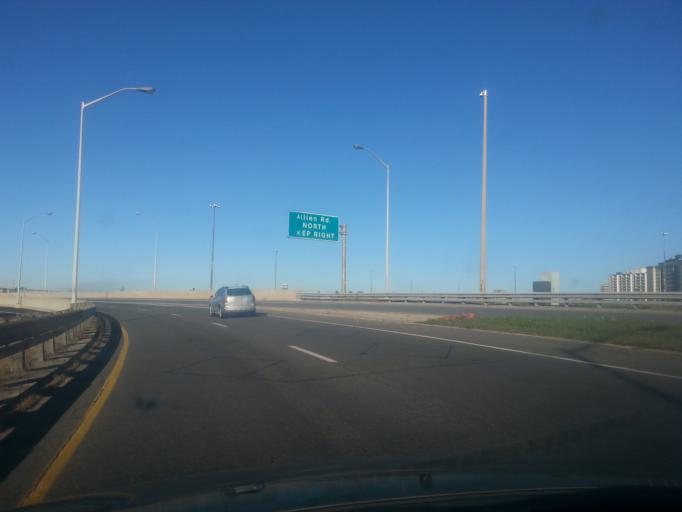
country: CA
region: Ontario
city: Toronto
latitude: 43.7293
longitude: -79.4468
